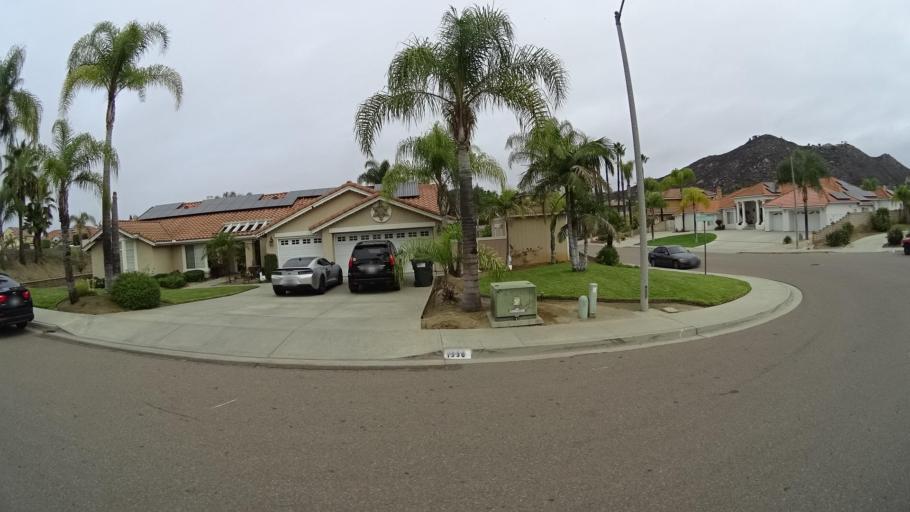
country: US
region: California
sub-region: San Diego County
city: Rancho San Diego
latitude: 32.7609
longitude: -116.9119
